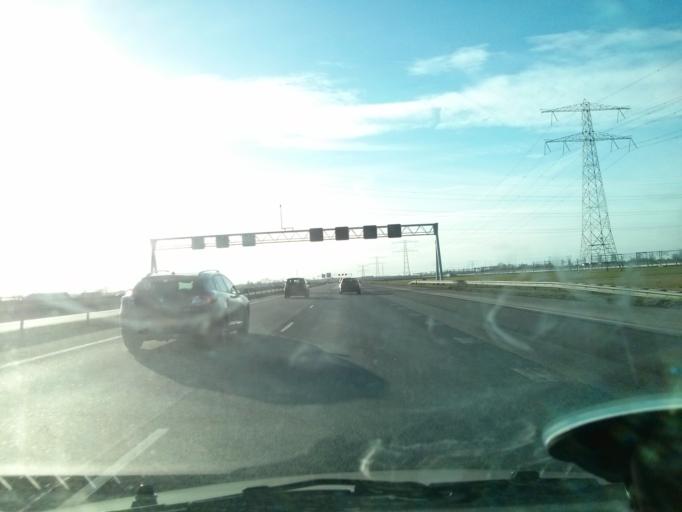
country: NL
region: Gelderland
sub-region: Gemeente Overbetuwe
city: Oosterhout
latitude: 51.8941
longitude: 5.8355
